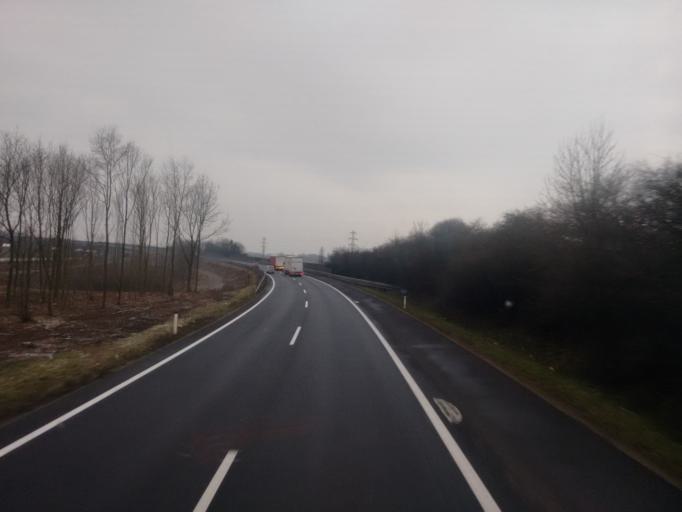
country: AT
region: Upper Austria
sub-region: Wels Stadt
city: Wels
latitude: 48.1815
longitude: 14.0005
